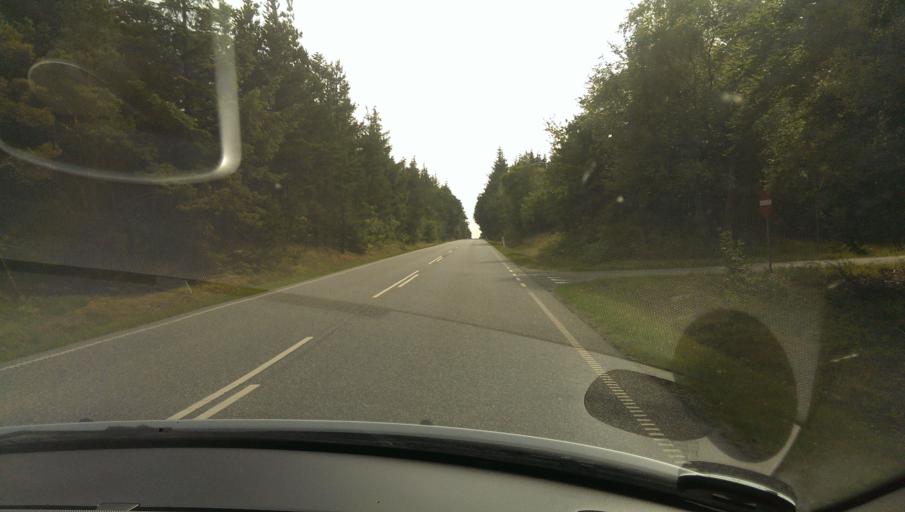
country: DK
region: Central Jutland
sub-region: Holstebro Kommune
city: Ulfborg
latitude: 56.2869
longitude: 8.1825
